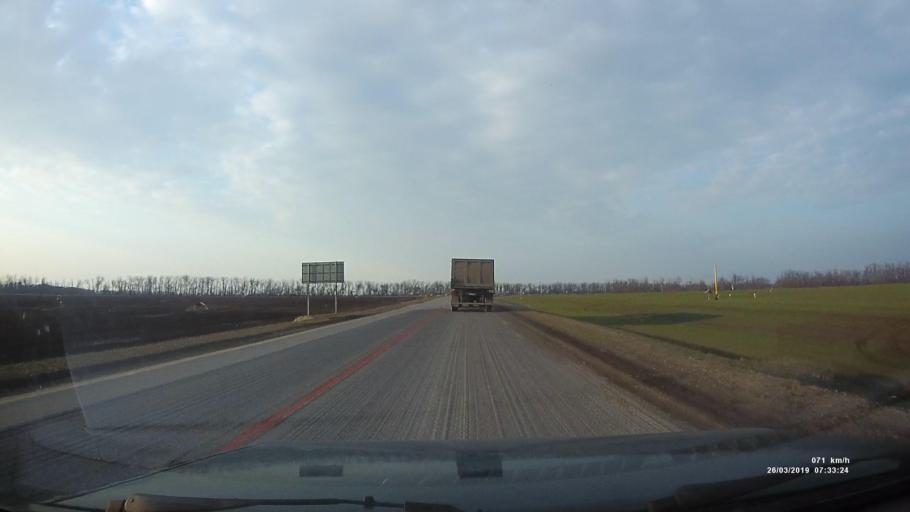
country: RU
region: Rostov
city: Novobessergenovka
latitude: 47.2156
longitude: 38.7704
